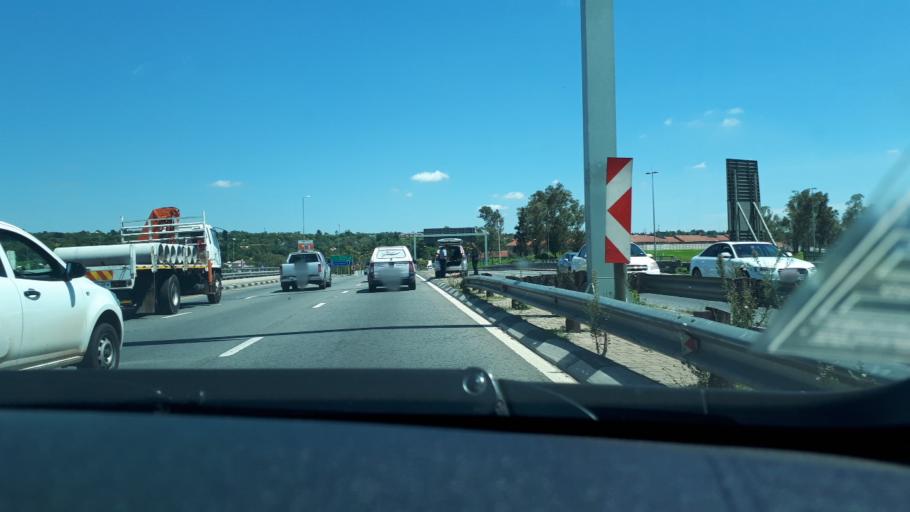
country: ZA
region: Gauteng
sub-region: City of Johannesburg Metropolitan Municipality
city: Roodepoort
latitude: -26.0731
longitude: 27.9740
